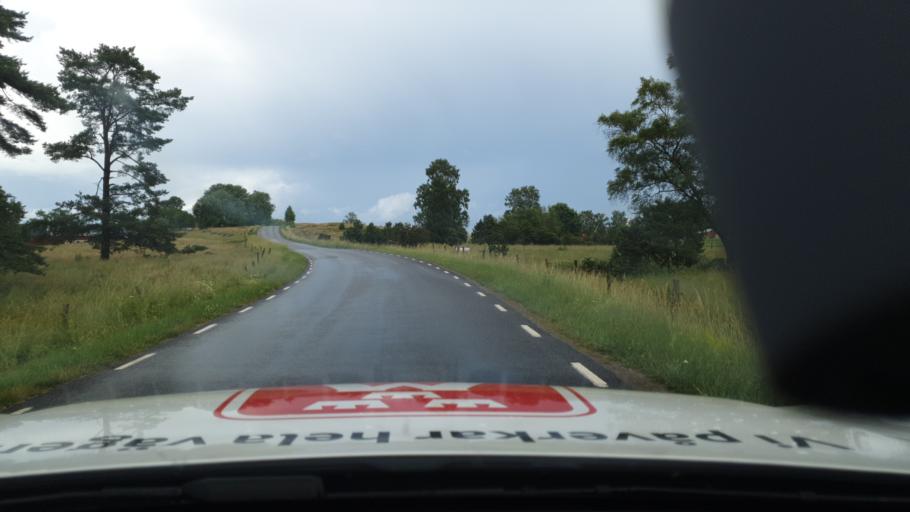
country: SE
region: Vaestra Goetaland
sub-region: Falkopings Kommun
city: Falkoeping
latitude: 58.0658
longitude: 13.6298
